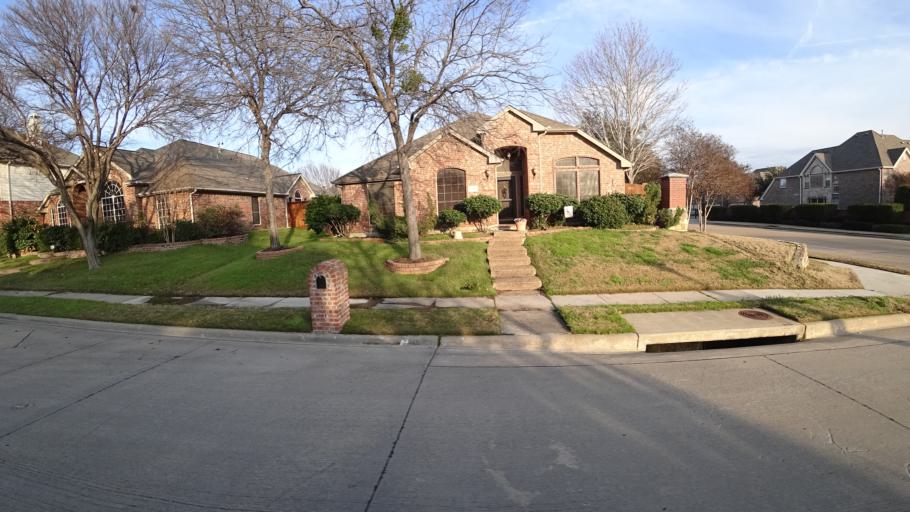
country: US
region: Texas
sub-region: Dallas County
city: Coppell
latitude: 32.9896
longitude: -96.9902
